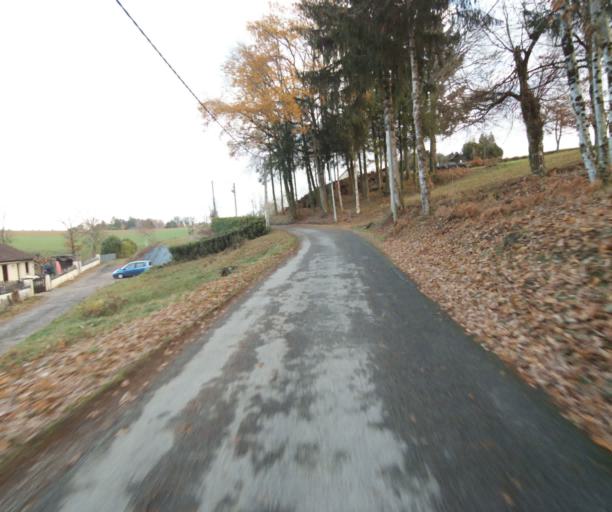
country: FR
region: Limousin
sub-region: Departement de la Correze
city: Laguenne
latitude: 45.2302
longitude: 1.7735
